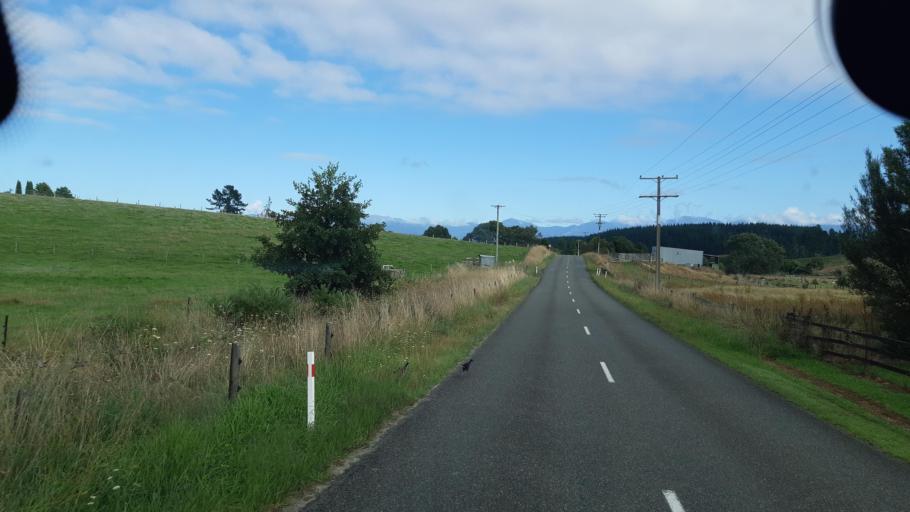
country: NZ
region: Tasman
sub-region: Tasman District
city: Mapua
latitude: -41.2432
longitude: 173.0438
